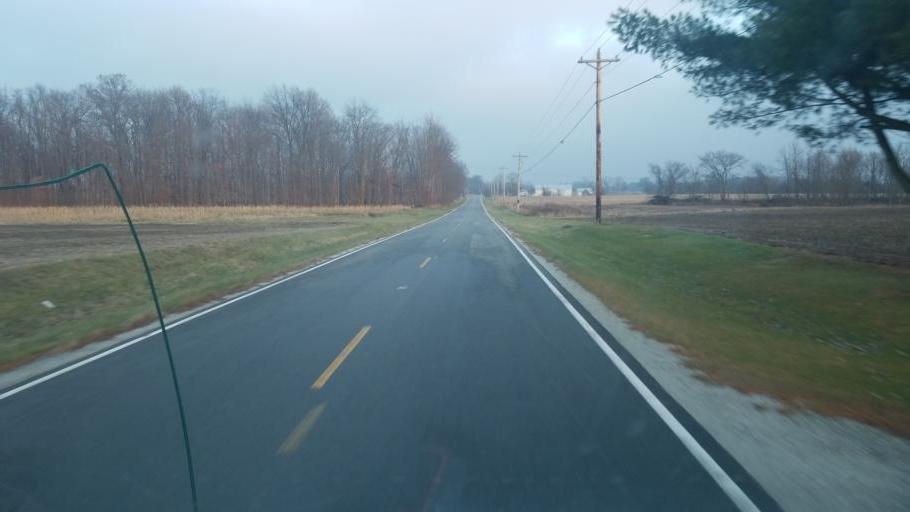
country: US
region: Ohio
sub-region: Wyandot County
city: Carey
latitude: 40.9999
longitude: -83.2827
